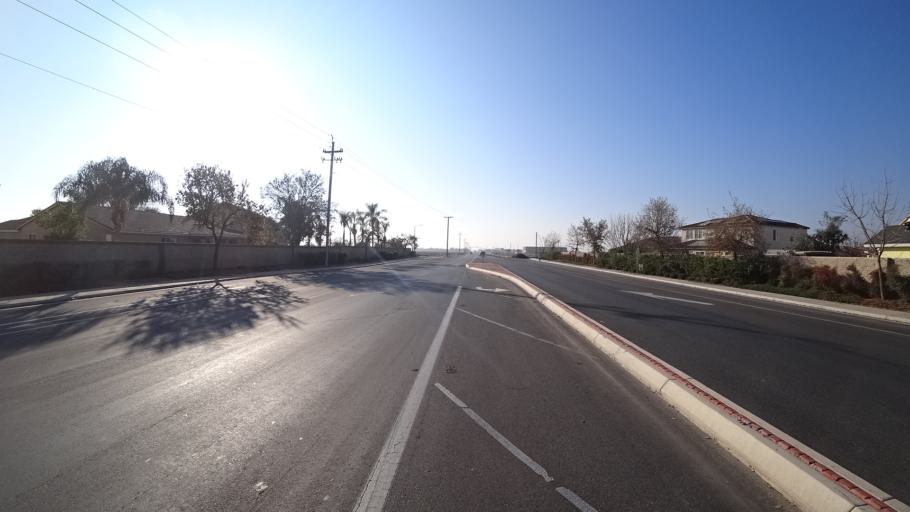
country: US
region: California
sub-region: Kern County
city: Greenacres
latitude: 35.3006
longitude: -119.1099
